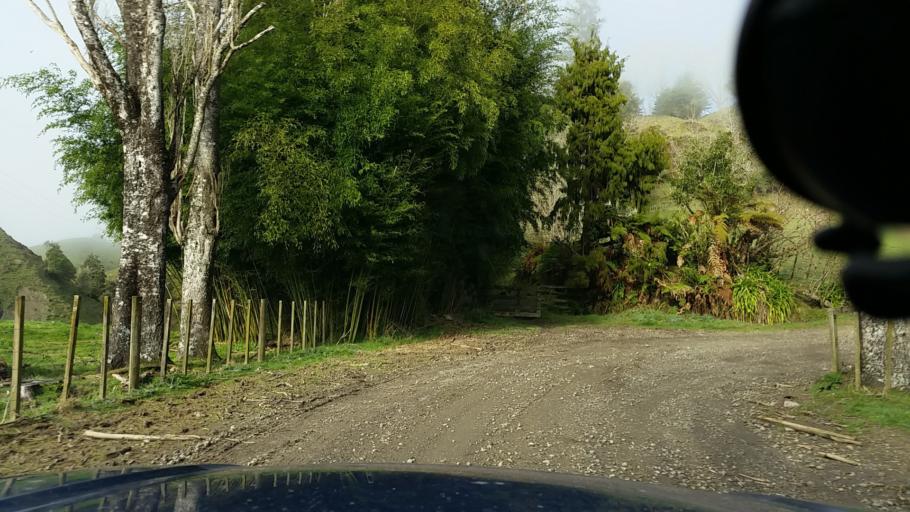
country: NZ
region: Taranaki
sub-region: New Plymouth District
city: Waitara
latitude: -39.0046
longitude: 174.7643
